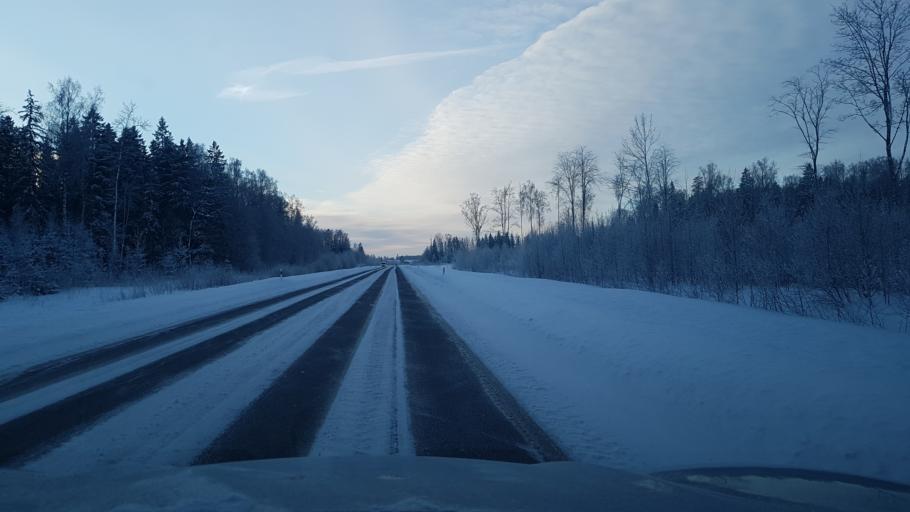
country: EE
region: Ida-Virumaa
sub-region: Johvi vald
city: Johvi
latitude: 59.3468
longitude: 27.4677
